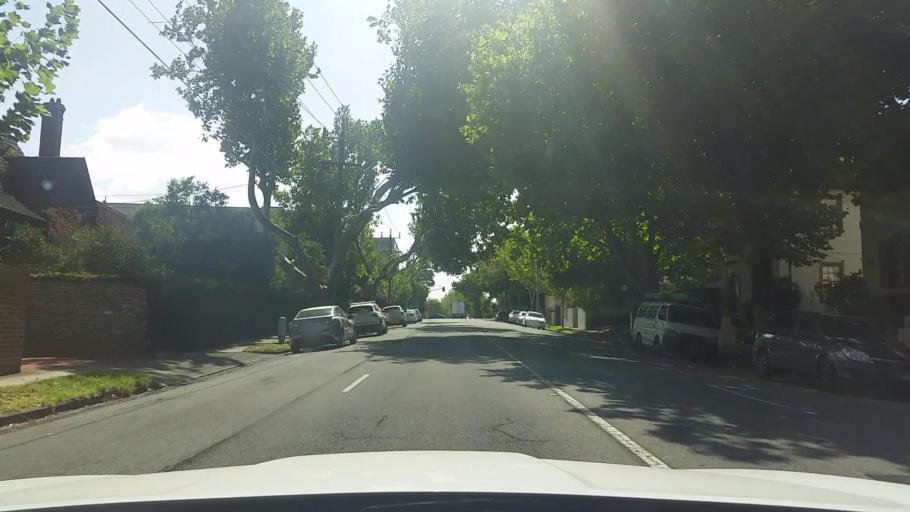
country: AU
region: Victoria
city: Toorak
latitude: -37.8433
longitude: 145.0135
